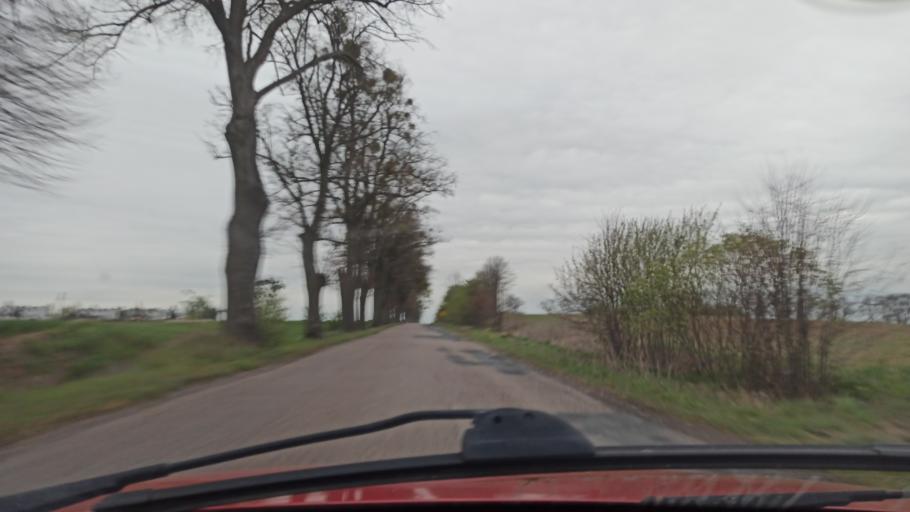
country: PL
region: Pomeranian Voivodeship
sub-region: Powiat kwidzynski
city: Gardeja
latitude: 53.5706
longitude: 18.9915
